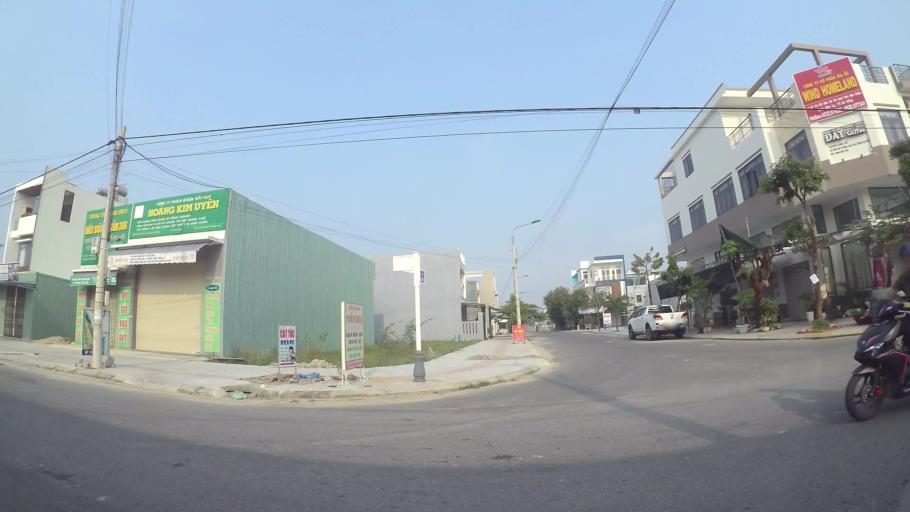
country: VN
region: Da Nang
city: Cam Le
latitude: 16.0063
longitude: 108.2279
